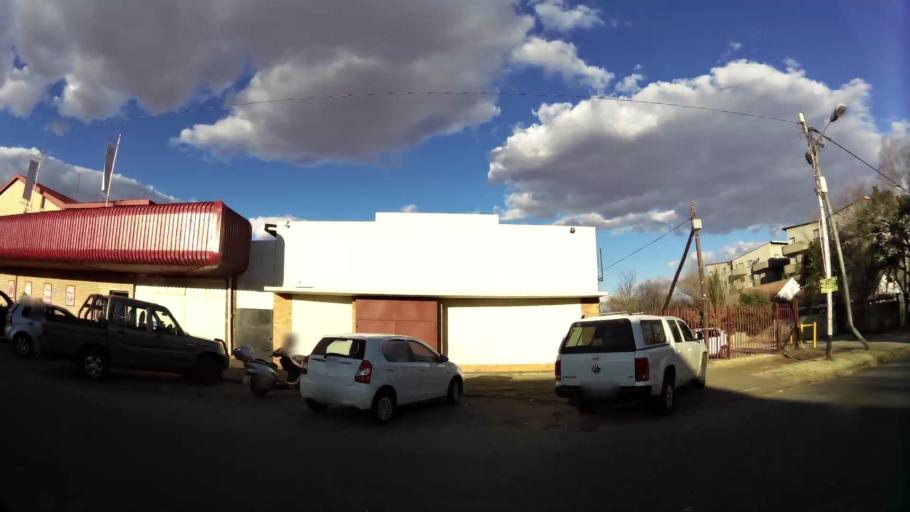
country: ZA
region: North-West
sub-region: Dr Kenneth Kaunda District Municipality
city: Potchefstroom
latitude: -26.7003
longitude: 27.0888
